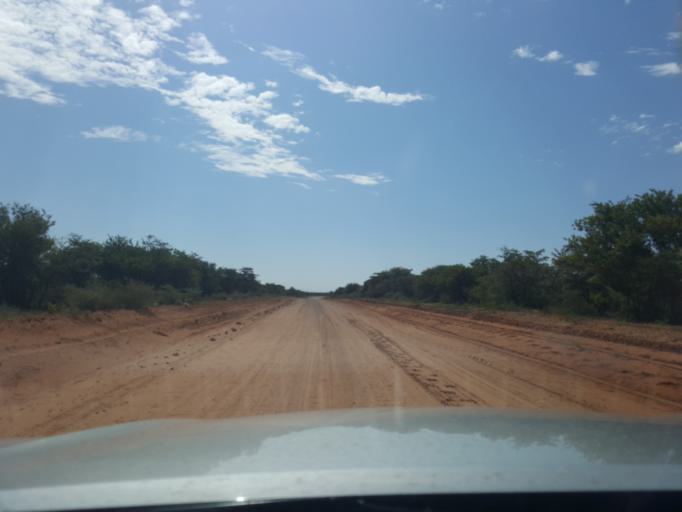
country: BW
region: Kweneng
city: Khudumelapye
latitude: -23.8055
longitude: 24.8133
